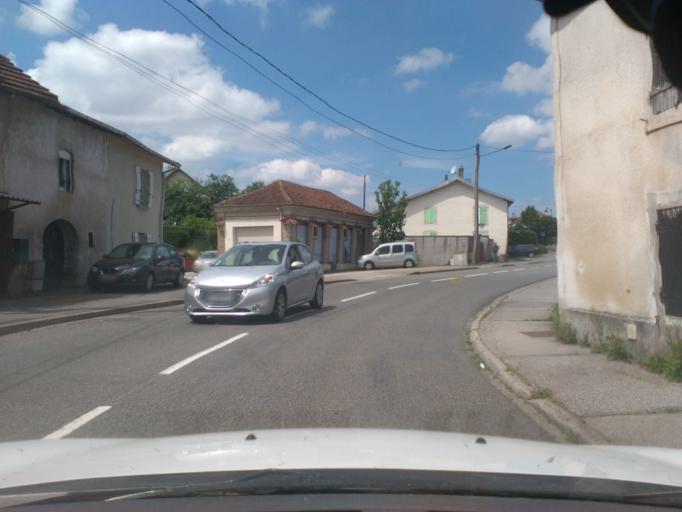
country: FR
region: Lorraine
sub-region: Departement des Vosges
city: Deyvillers
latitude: 48.1993
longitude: 6.5177
